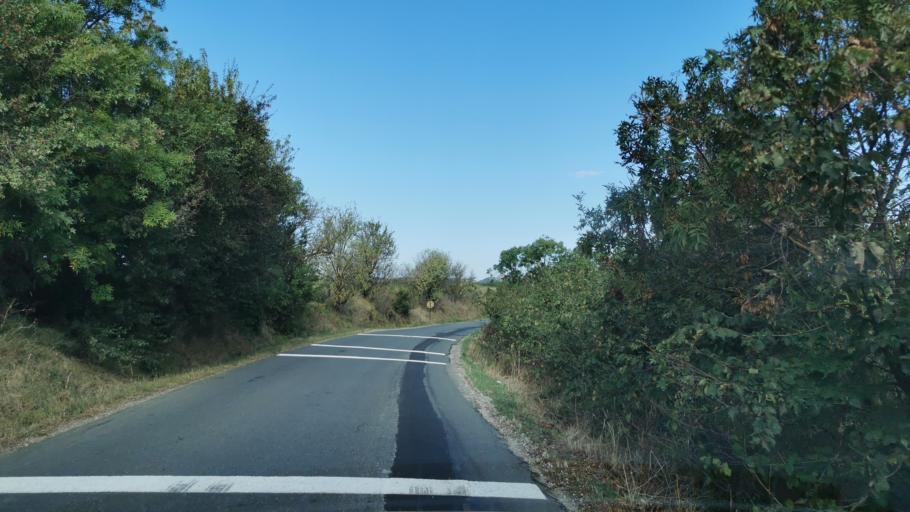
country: FR
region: Languedoc-Roussillon
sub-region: Departement de l'Aude
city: Narbonne
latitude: 43.1435
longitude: 3.0170
